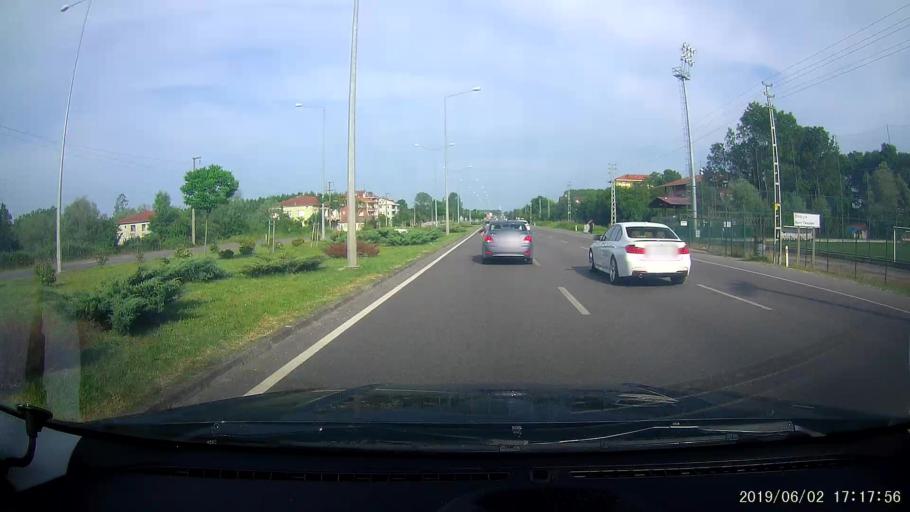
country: TR
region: Samsun
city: Dikbiyik
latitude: 41.2262
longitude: 36.5896
